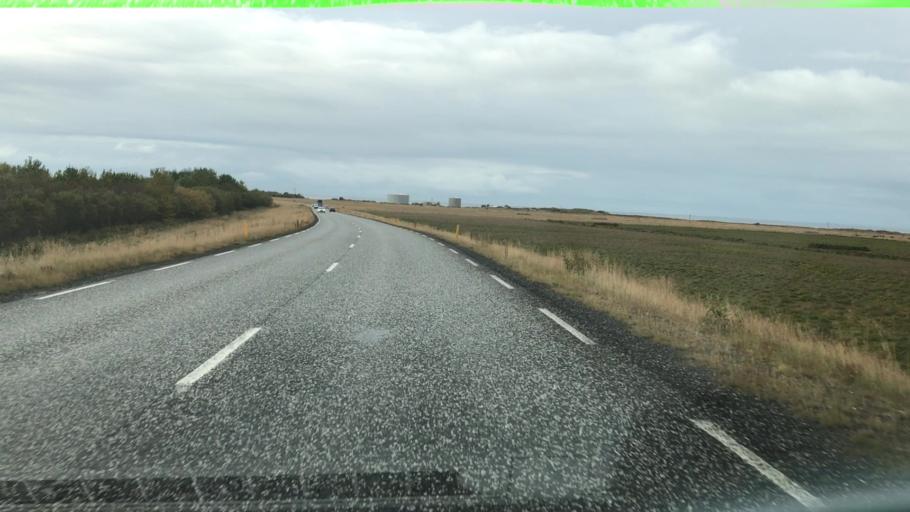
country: IS
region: West
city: Akranes
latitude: 64.3255
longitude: -22.0179
